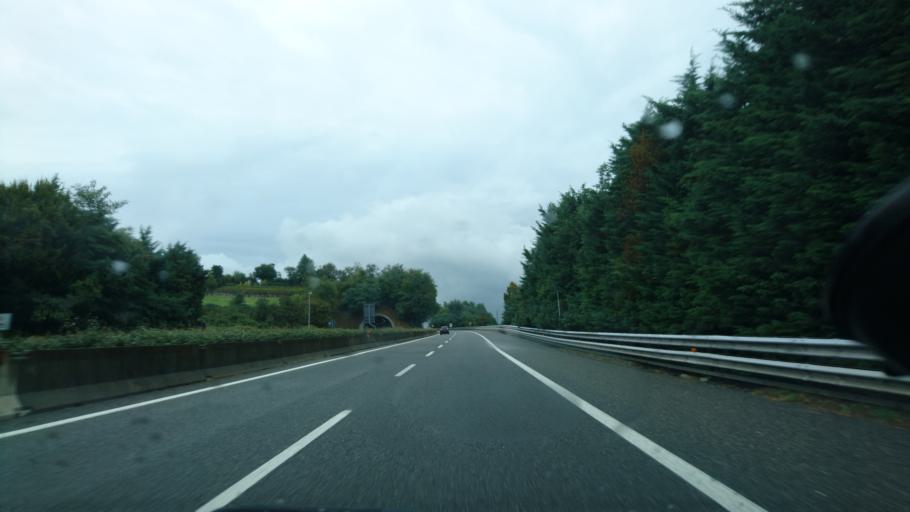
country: IT
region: Piedmont
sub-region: Provincia di Novara
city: Nebbiuno
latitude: 45.8068
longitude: 8.5315
